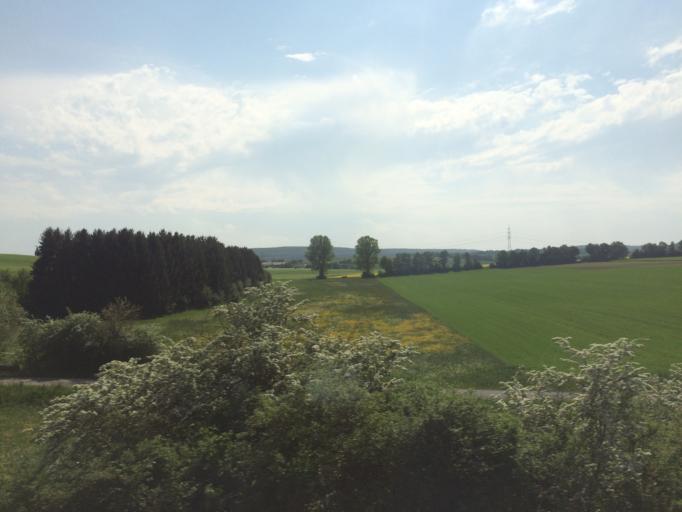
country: DE
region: Bavaria
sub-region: Regierungsbezirk Mittelfranken
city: Langenfeld
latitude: 49.6099
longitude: 10.5263
